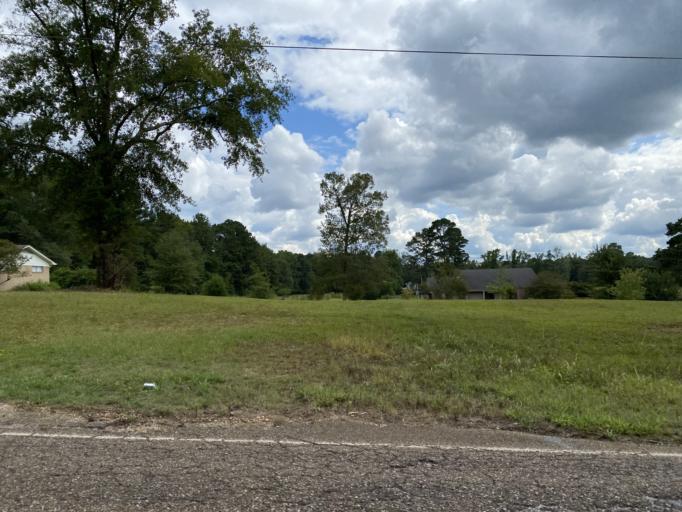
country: US
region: Mississippi
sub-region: Monroe County
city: Amory
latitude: 33.9717
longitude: -88.4491
